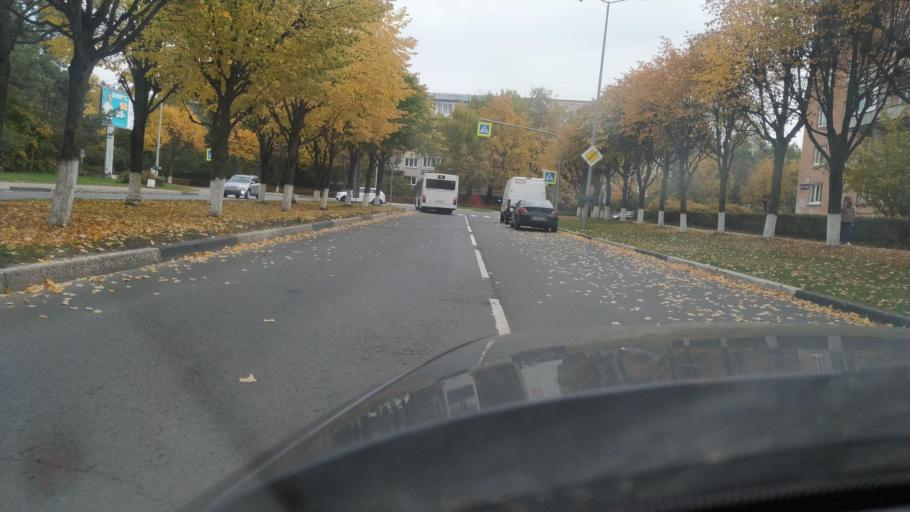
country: RU
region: Leningrad
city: Sosnovyy Bor
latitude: 59.8935
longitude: 29.0867
